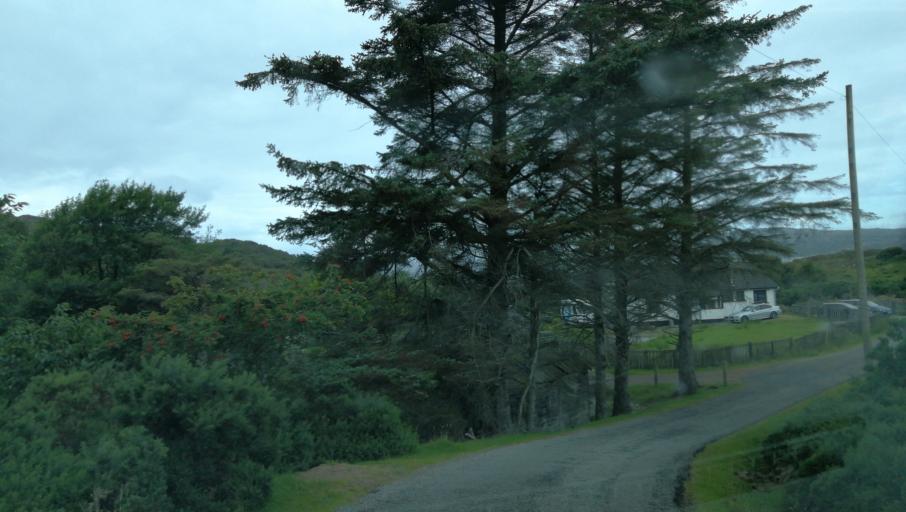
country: GB
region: Scotland
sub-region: Highland
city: Ullapool
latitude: 58.1342
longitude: -5.2621
